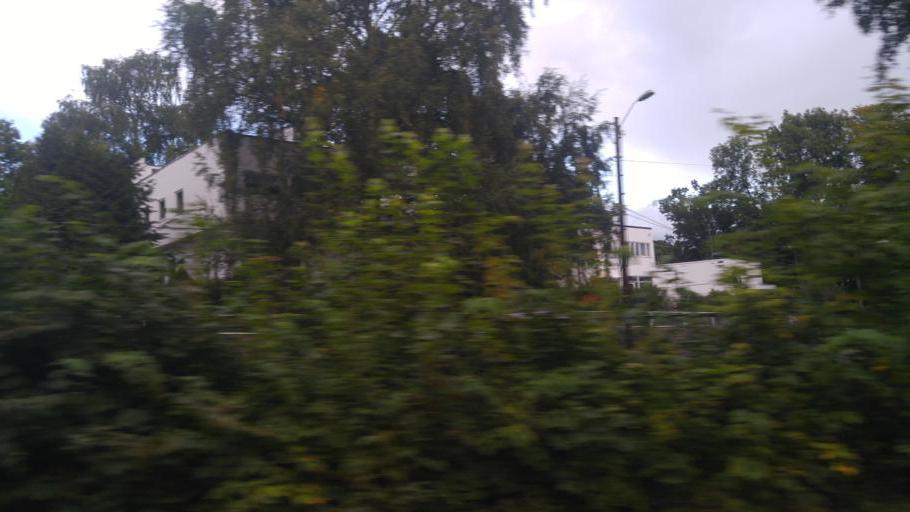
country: NO
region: Oslo
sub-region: Oslo
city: Sjolyststranda
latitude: 59.9364
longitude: 10.7077
